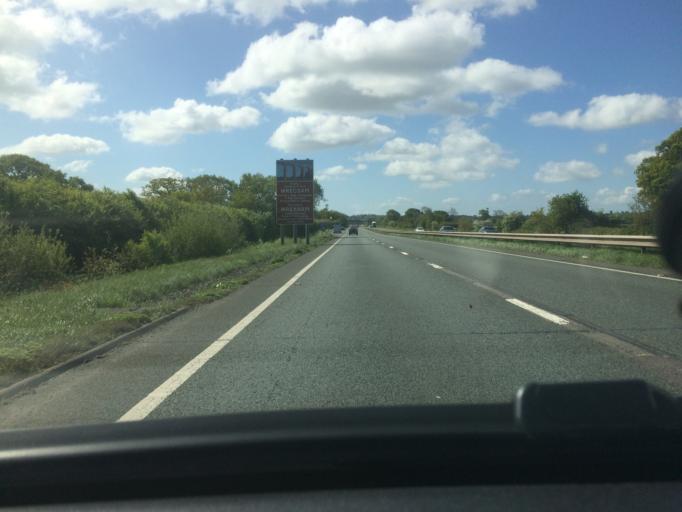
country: GB
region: Wales
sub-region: Wrexham
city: Rossett
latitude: 53.1270
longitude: -2.9484
